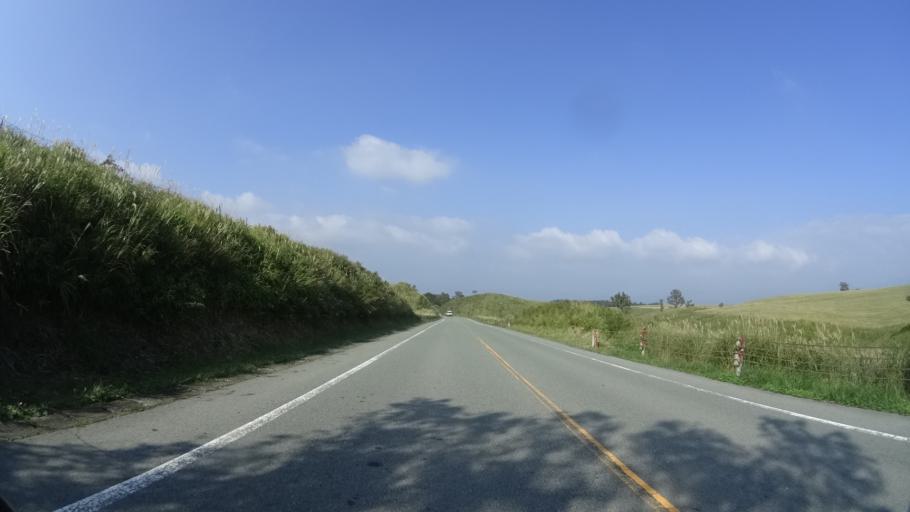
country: JP
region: Kumamoto
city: Aso
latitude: 33.0219
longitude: 131.0680
